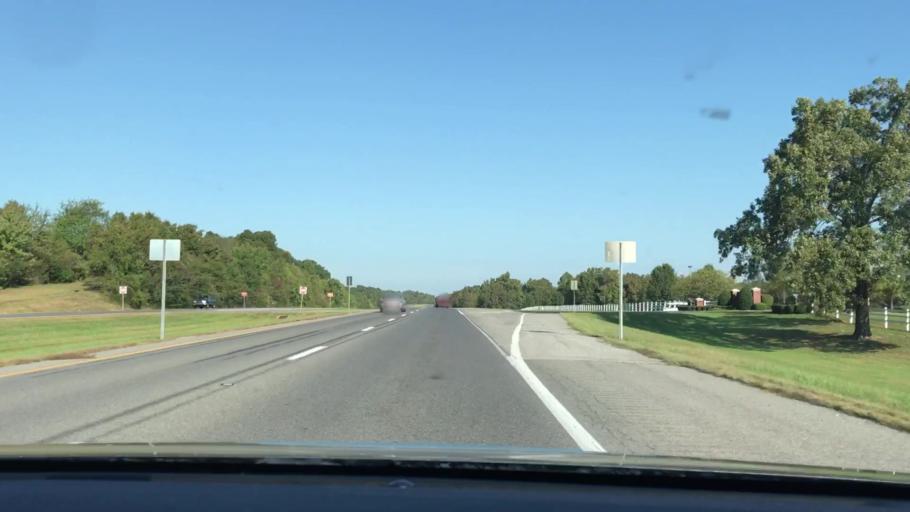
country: US
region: Kentucky
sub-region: Marshall County
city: Benton
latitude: 36.7687
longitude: -88.3134
